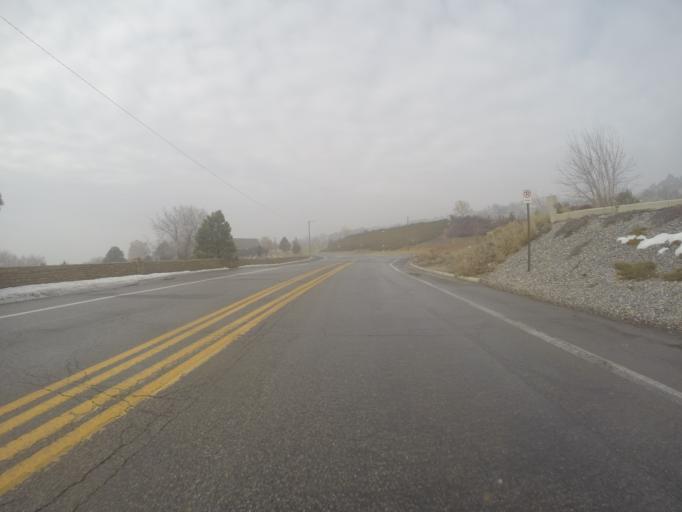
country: US
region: Utah
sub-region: Salt Lake County
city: Salt Lake City
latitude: 40.7811
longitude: -111.8622
